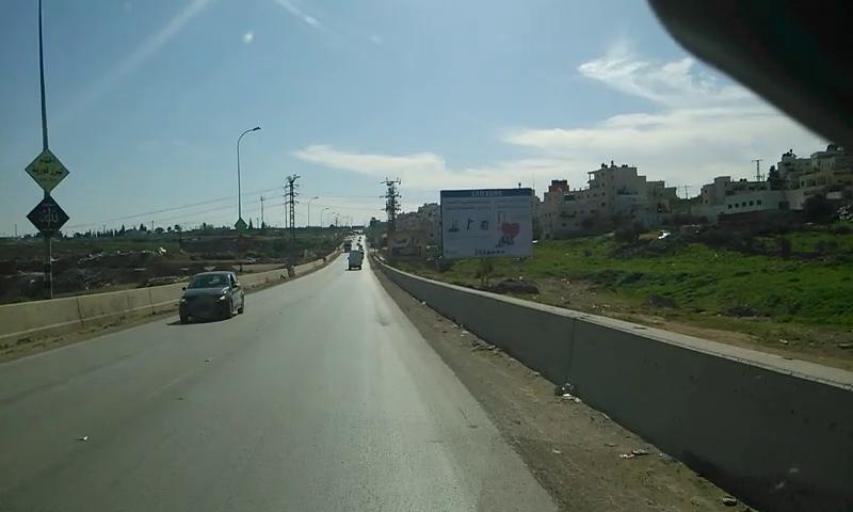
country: PS
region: West Bank
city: Ar Ram wa Dahiyat al Barid
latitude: 31.8582
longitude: 35.2354
